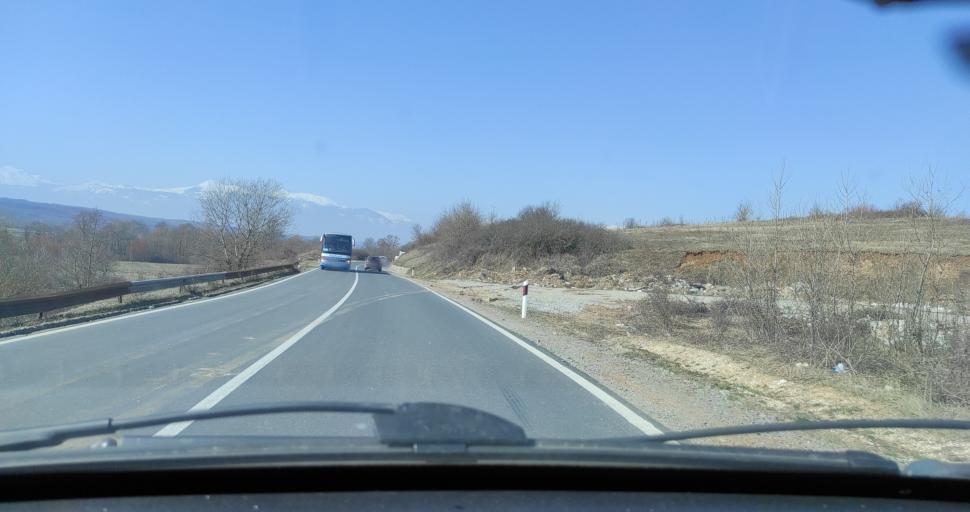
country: XK
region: Pec
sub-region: Komuna e Klines
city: Klina
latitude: 42.5933
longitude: 20.5463
